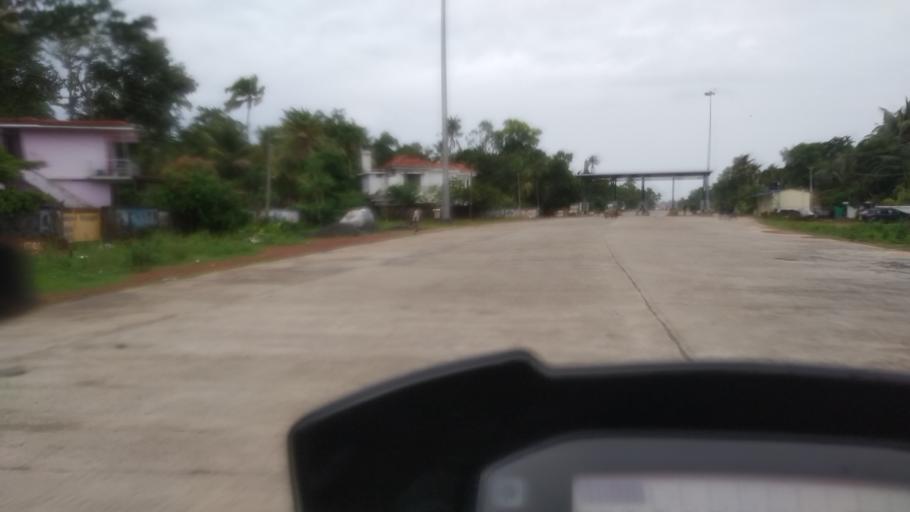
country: IN
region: Kerala
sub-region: Alappuzha
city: Alleppey
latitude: 9.5128
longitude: 76.3270
